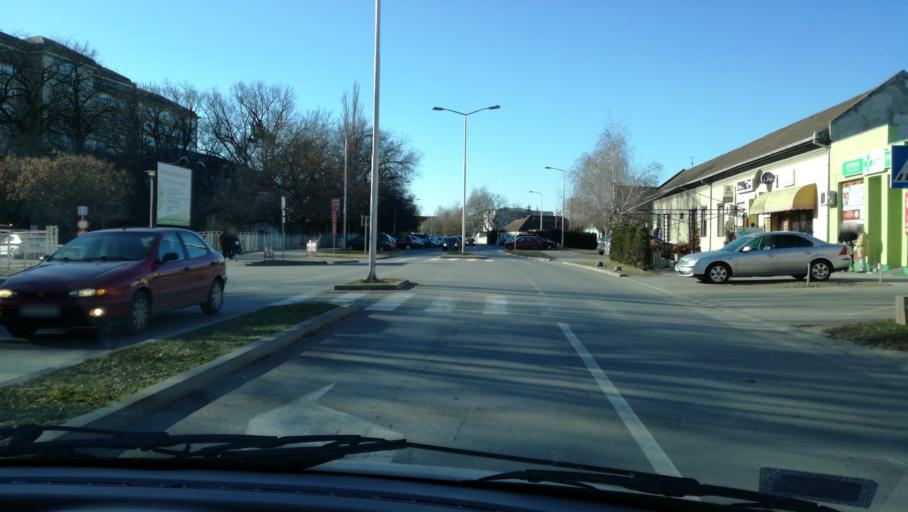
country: RS
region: Autonomna Pokrajina Vojvodina
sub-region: Severnobacki Okrug
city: Subotica
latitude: 46.0826
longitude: 19.6724
